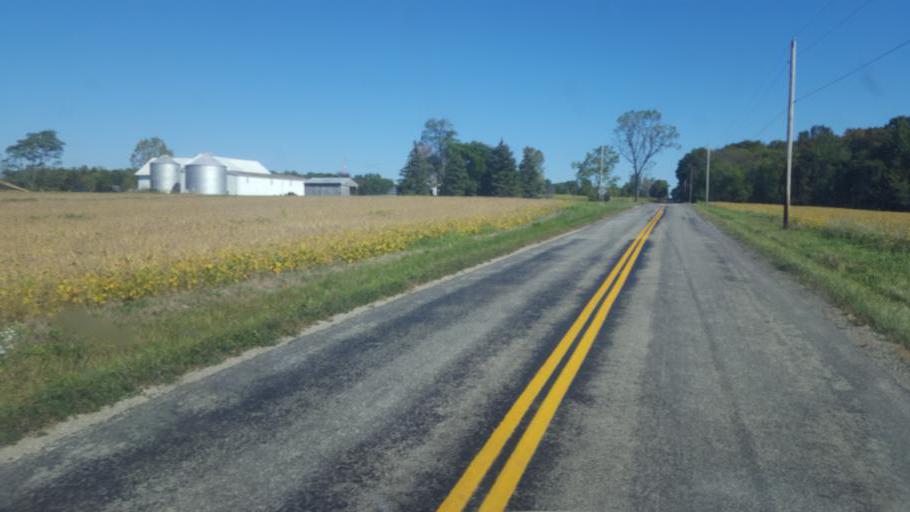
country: US
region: Ohio
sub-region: Huron County
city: New London
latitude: 40.9929
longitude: -82.3498
